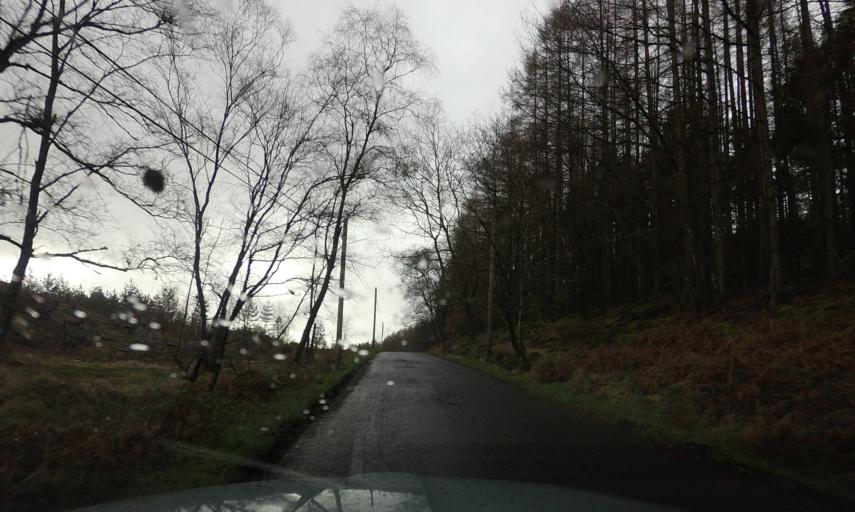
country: GB
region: Scotland
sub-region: West Dunbartonshire
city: Balloch
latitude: 56.1464
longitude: -4.6390
